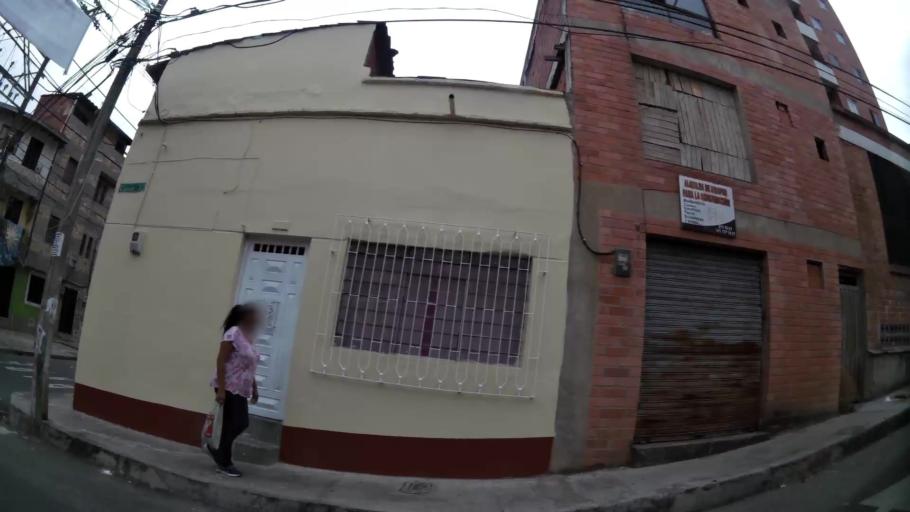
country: CO
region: Antioquia
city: Medellin
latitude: 6.2398
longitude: -75.5553
